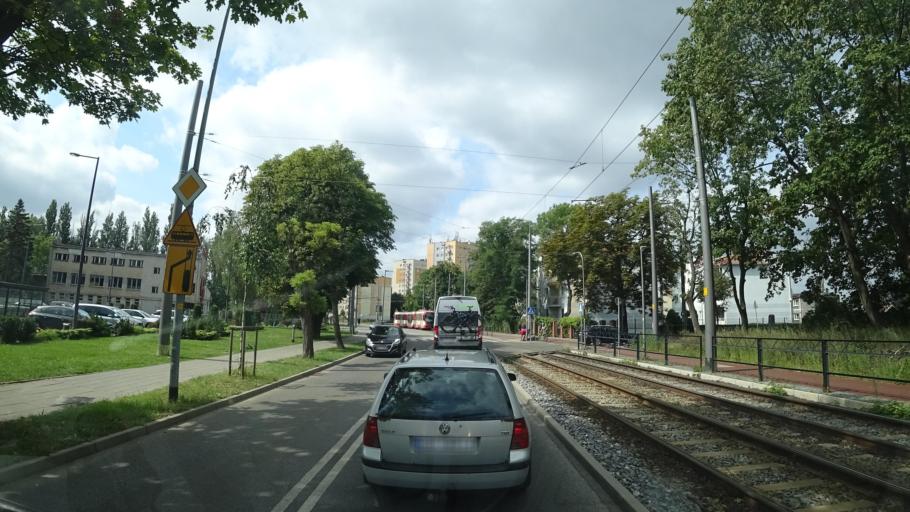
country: PL
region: Pomeranian Voivodeship
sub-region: Gdansk
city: Gdansk
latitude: 54.3640
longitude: 18.7170
